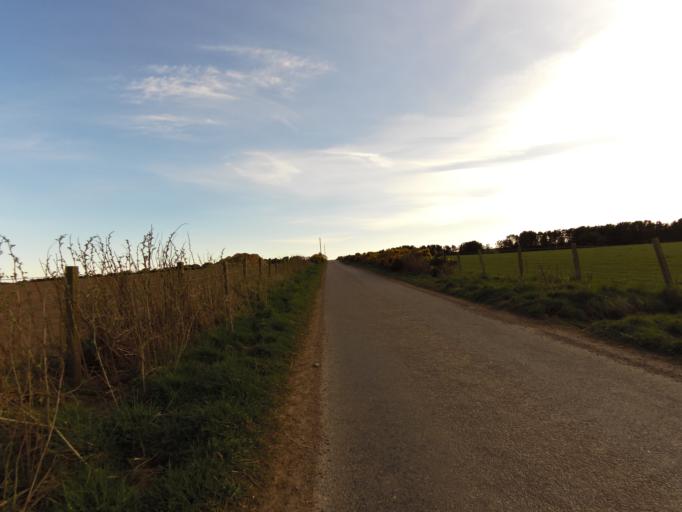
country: GB
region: Scotland
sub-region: Aberdeenshire
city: Stonehaven
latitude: 56.9405
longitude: -2.2217
